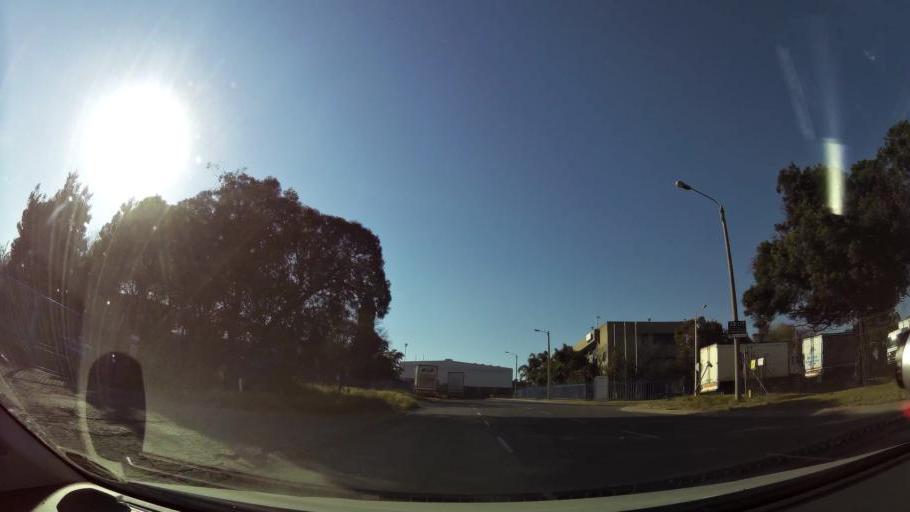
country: ZA
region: Gauteng
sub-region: City of Johannesburg Metropolitan Municipality
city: Modderfontein
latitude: -26.0610
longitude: 28.1740
